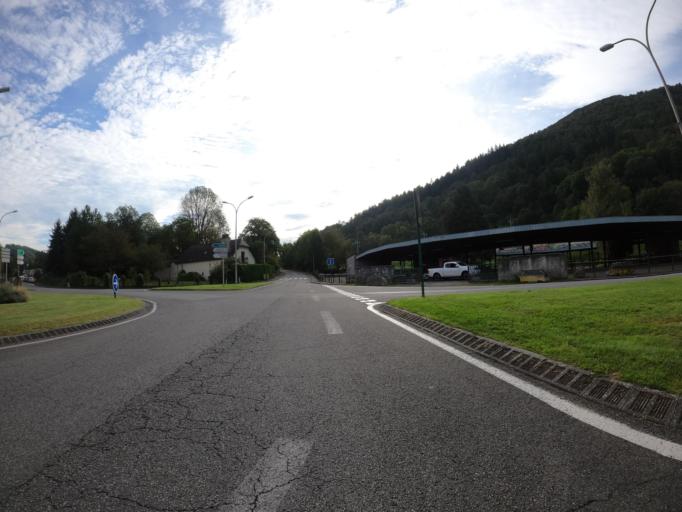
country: FR
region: Midi-Pyrenees
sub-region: Departement des Hautes-Pyrenees
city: Lourdes
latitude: 43.0956
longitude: -0.0349
